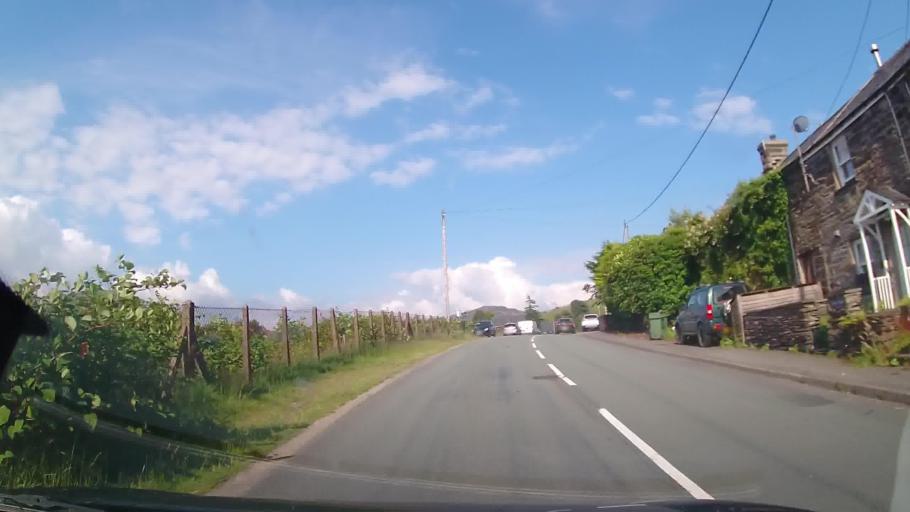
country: GB
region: Wales
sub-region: Gwynedd
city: Ffestiniog
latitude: 52.9606
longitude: -3.9254
